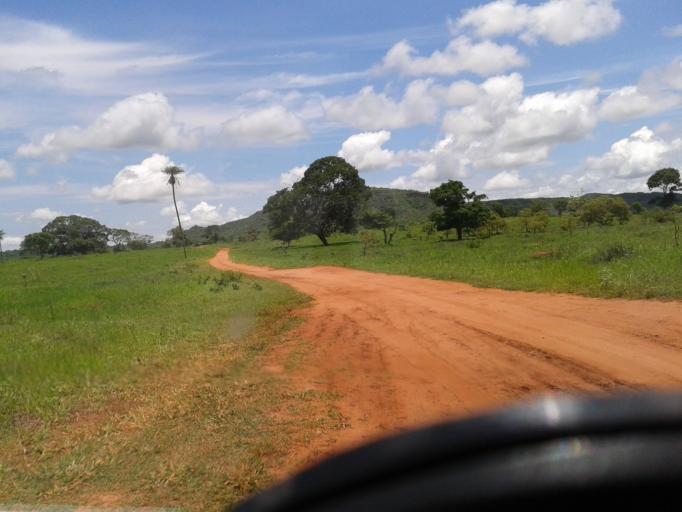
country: BR
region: Minas Gerais
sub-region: Santa Vitoria
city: Santa Vitoria
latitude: -18.9939
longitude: -49.9084
